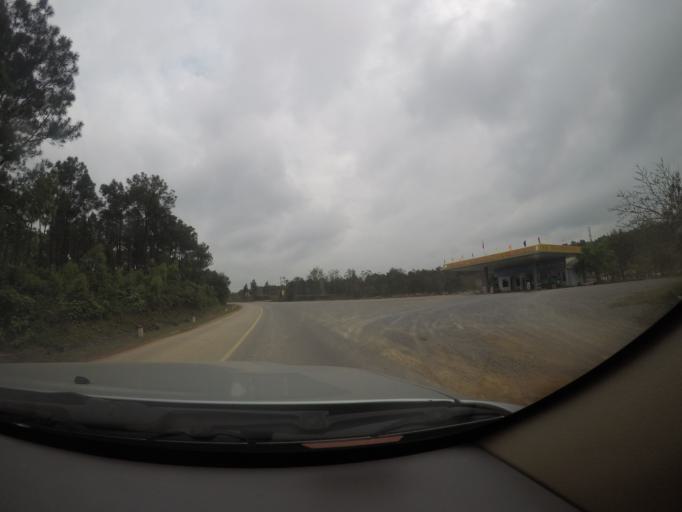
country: VN
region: Quang Binh
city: Quan Hau
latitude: 17.3865
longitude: 106.6110
